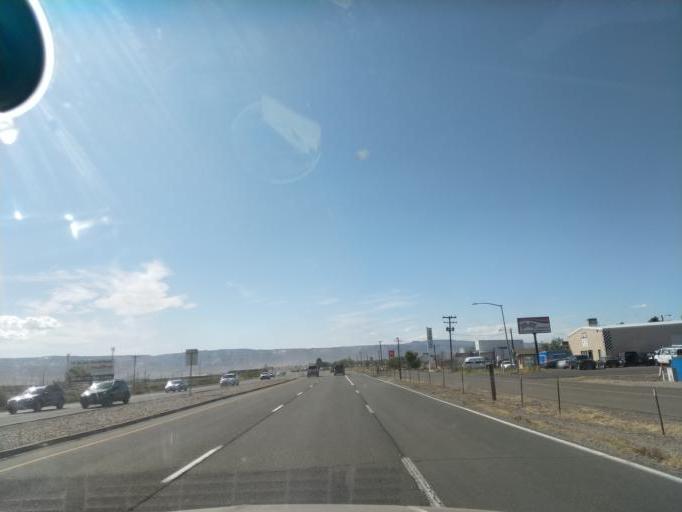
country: US
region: Colorado
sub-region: Mesa County
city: Grand Junction
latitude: 39.0709
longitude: -108.5256
